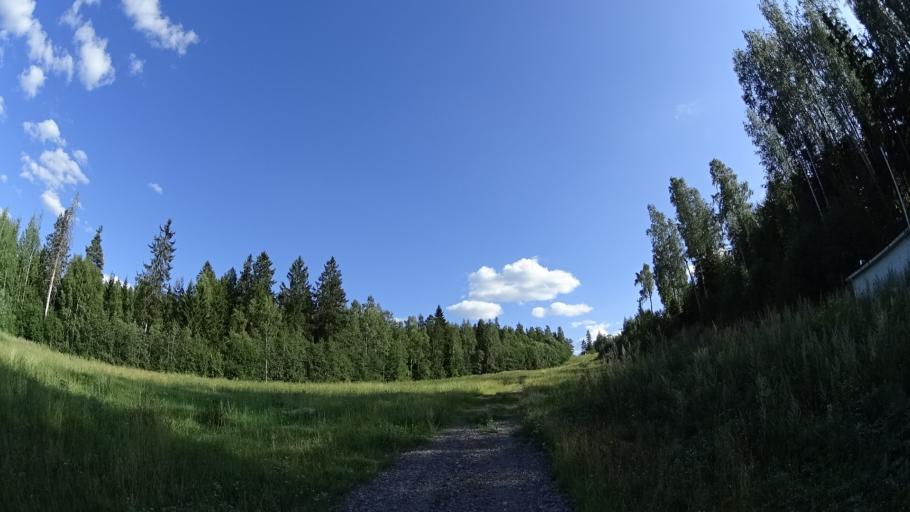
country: FI
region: Uusimaa
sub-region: Helsinki
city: Vihti
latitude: 60.3790
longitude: 24.3704
